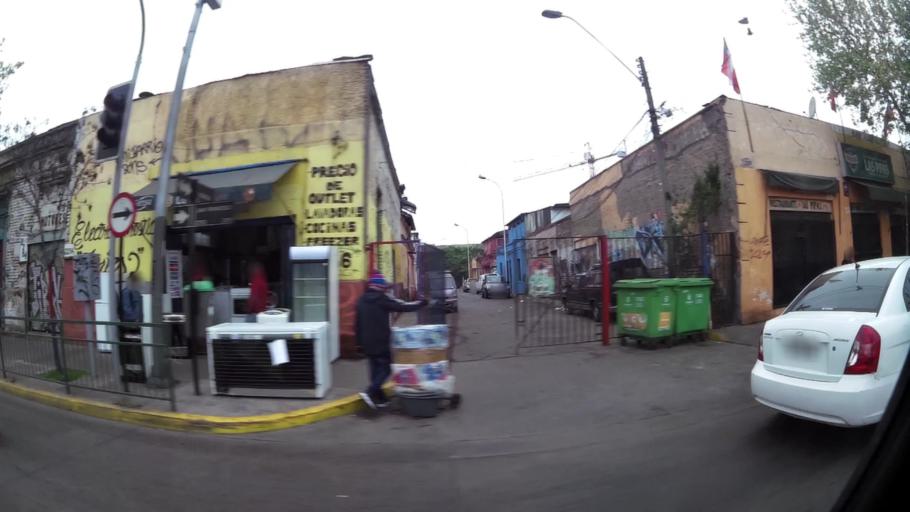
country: CL
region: Santiago Metropolitan
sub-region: Provincia de Santiago
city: Santiago
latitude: -33.4747
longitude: -70.6436
